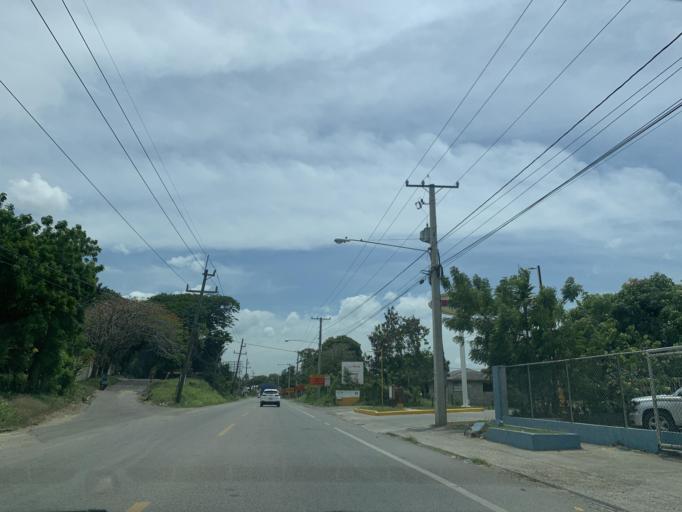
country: DO
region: Puerto Plata
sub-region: Puerto Plata
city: Puerto Plata
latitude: 19.7489
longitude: -70.5844
